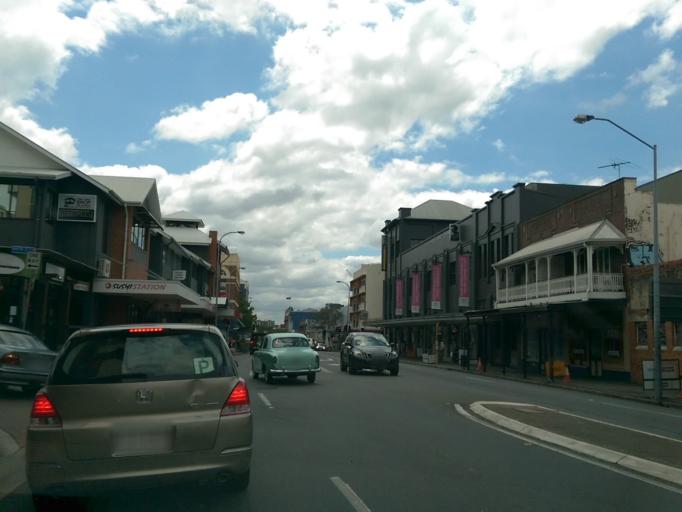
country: AU
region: Queensland
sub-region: Brisbane
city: Fortitude Valley
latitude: -27.4601
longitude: 153.0370
